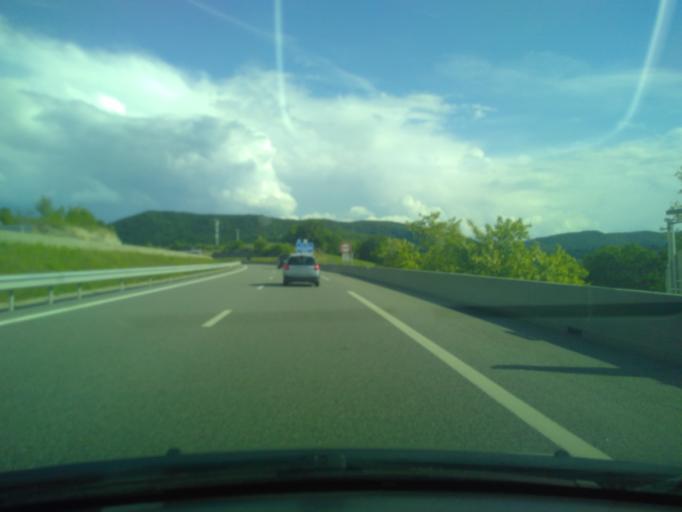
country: FR
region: Rhone-Alpes
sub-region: Departement de la Haute-Savoie
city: Cruseilles
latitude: 46.0207
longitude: 6.0990
